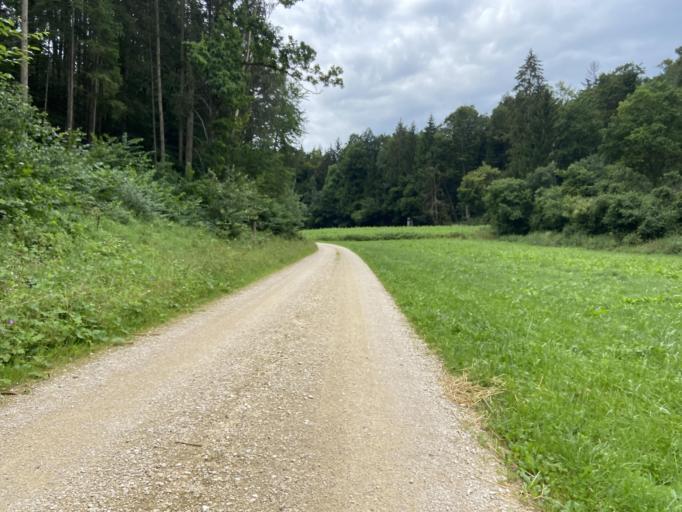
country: DE
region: Baden-Wuerttemberg
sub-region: Tuebingen Region
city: Bingen
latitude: 48.1252
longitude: 9.2754
